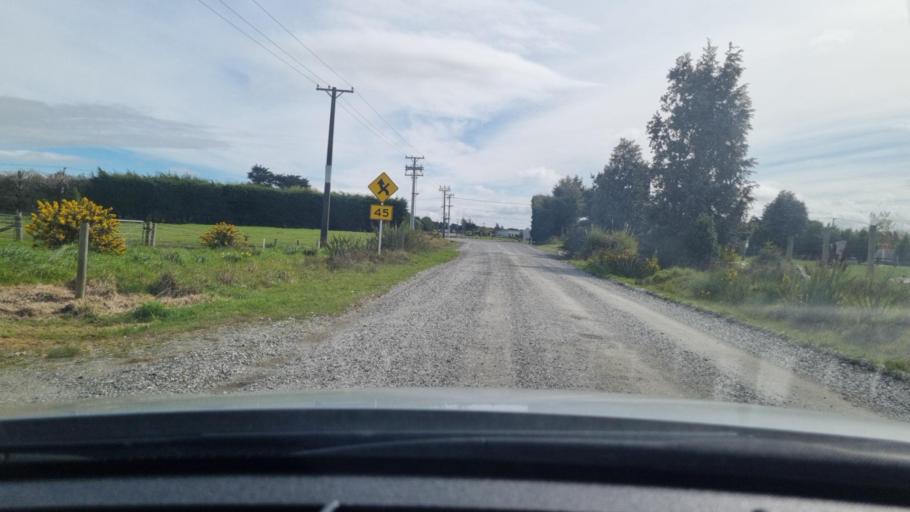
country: NZ
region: Southland
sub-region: Invercargill City
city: Invercargill
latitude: -46.4508
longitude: 168.3823
